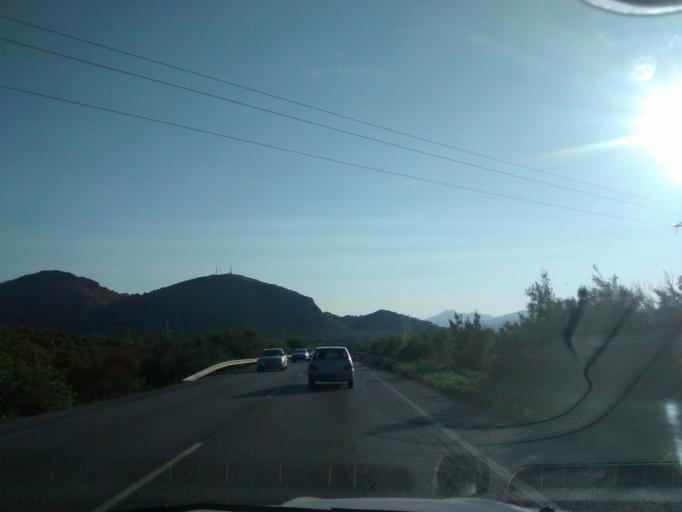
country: ES
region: Balearic Islands
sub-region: Illes Balears
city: Alcudia
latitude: 39.8449
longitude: 3.1168
